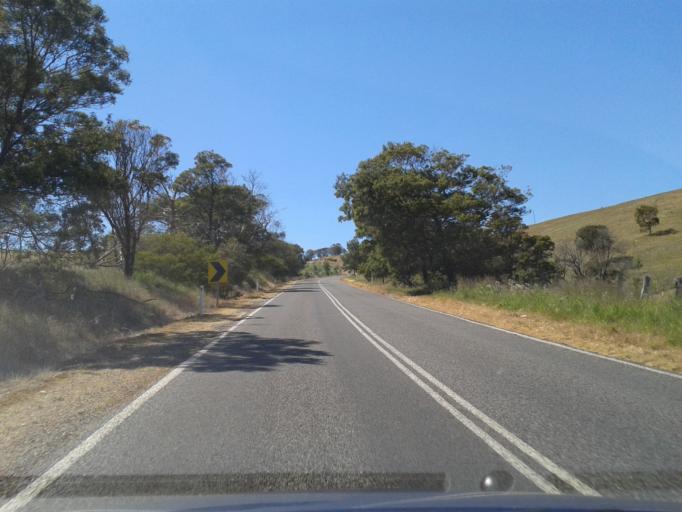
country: AU
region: Victoria
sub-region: Ararat
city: Ararat
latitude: -37.2944
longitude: 142.8534
